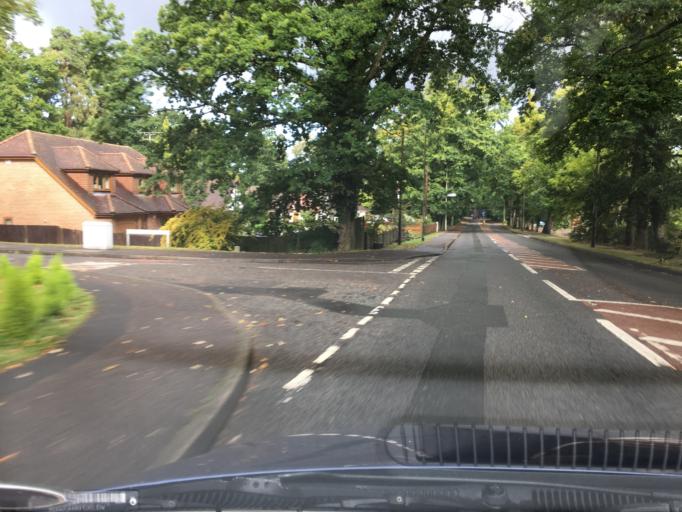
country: GB
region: England
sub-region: Bracknell Forest
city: Crowthorne
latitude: 51.3761
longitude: -0.8045
